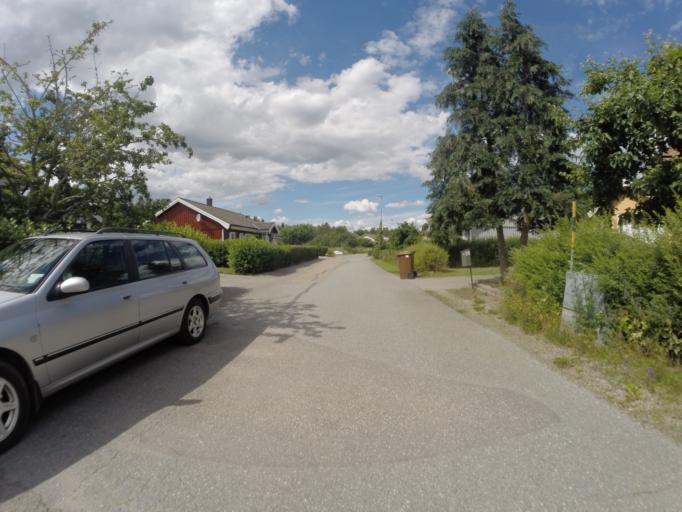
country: SE
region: Soedermanland
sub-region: Eskilstuna Kommun
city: Kvicksund
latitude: 59.4440
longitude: 16.3171
